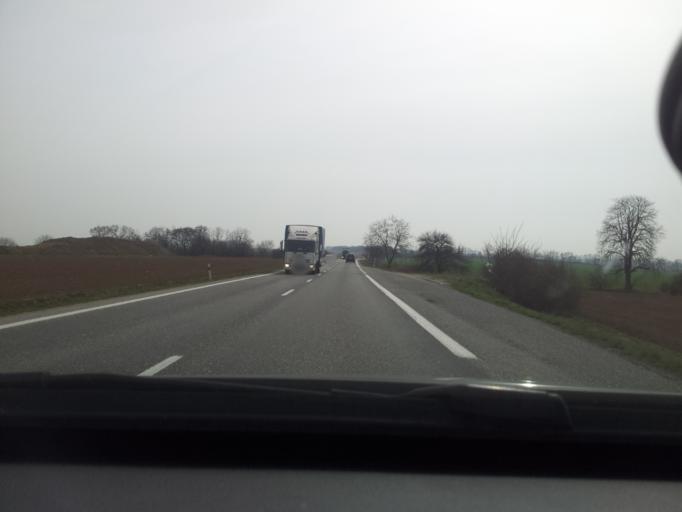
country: SK
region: Nitriansky
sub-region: Okres Nitra
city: Vrable
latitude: 48.2847
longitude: 18.2157
